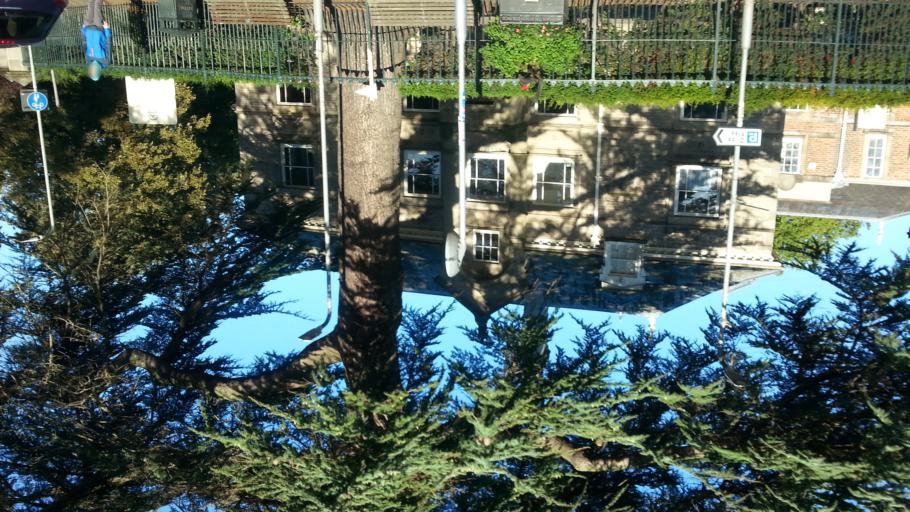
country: GB
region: Wales
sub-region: Monmouthshire
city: Monmouth
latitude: 51.8095
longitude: -2.7225
